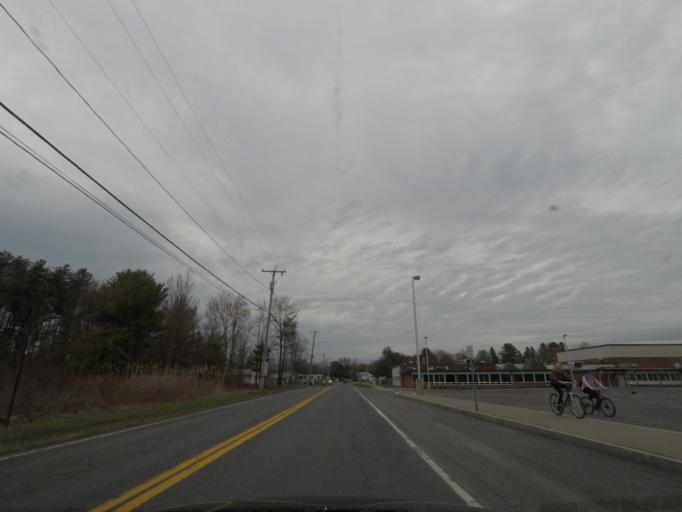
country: US
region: New York
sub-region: Albany County
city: Delmar
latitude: 42.6111
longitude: -73.8583
